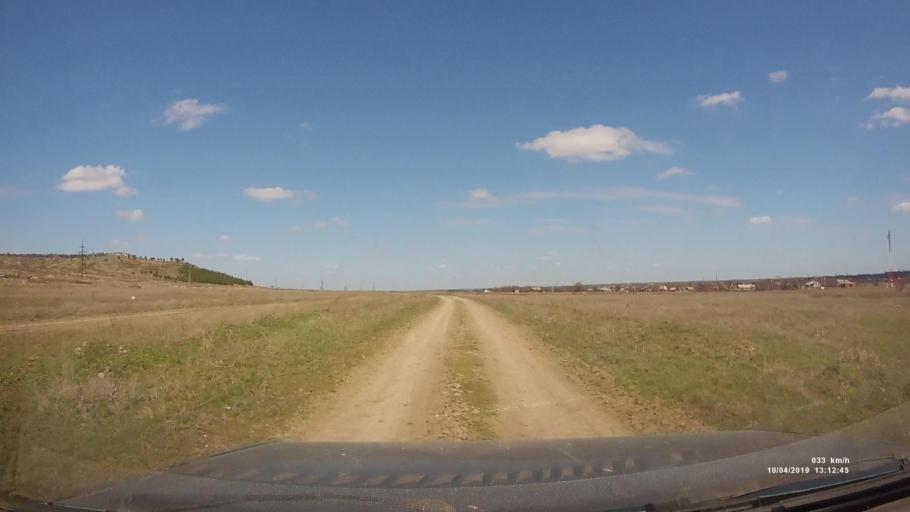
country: RU
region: Rostov
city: Masalovka
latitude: 48.4141
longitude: 40.2569
